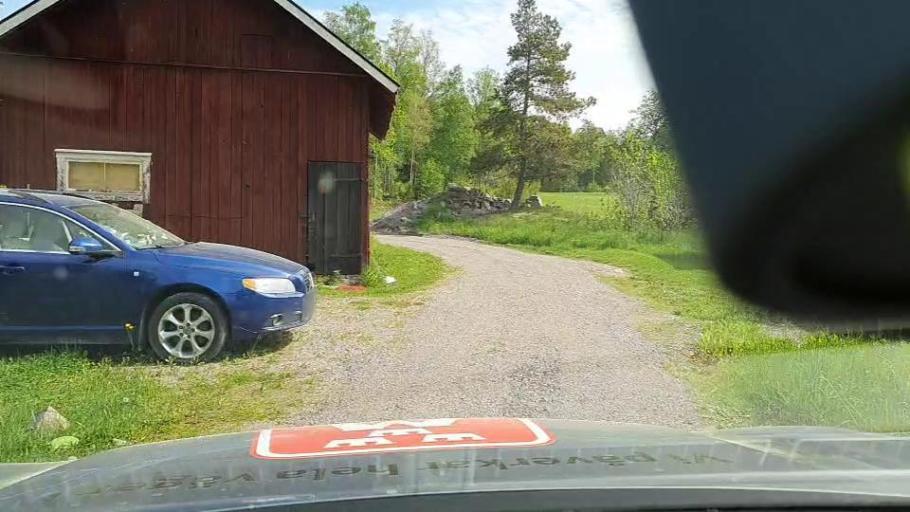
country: SE
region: Soedermanland
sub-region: Eskilstuna Kommun
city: Skogstorp
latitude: 59.2535
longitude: 16.5031
